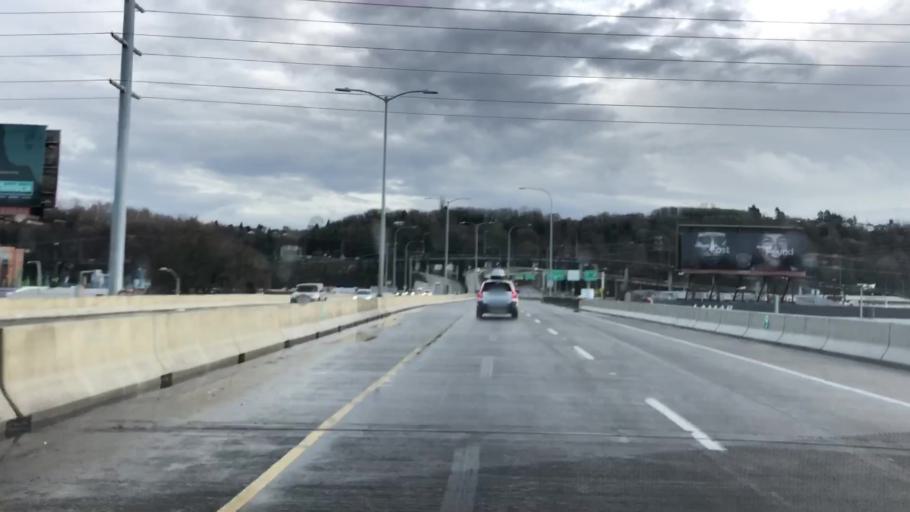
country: US
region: Washington
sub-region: King County
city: Seattle
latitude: 47.5716
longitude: -122.3282
